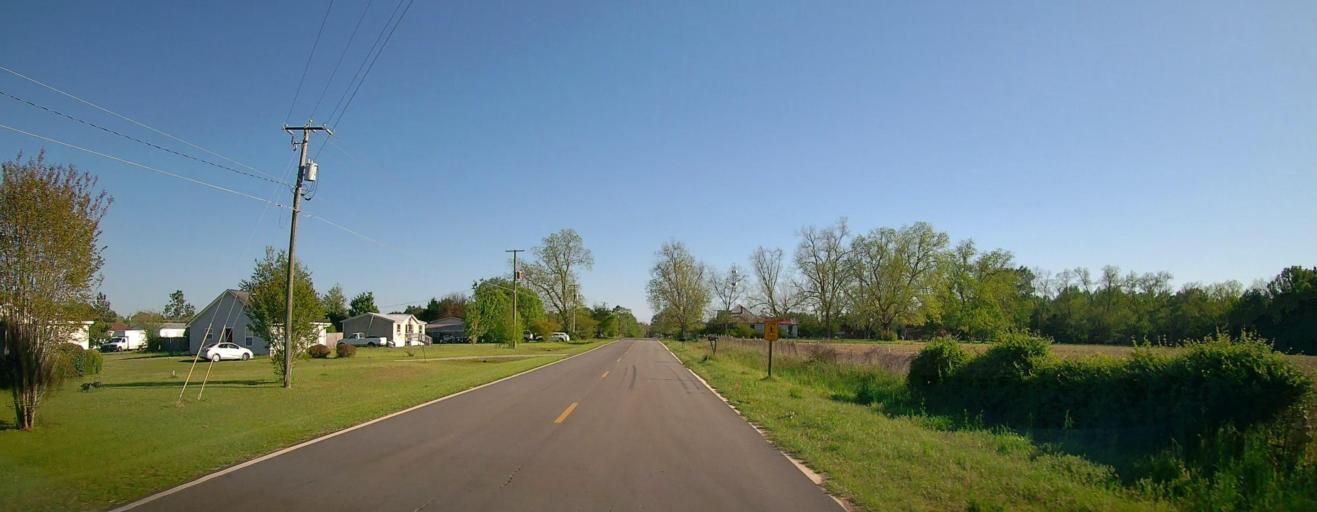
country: US
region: Georgia
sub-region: Ben Hill County
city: Fitzgerald
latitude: 31.7343
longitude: -83.2802
